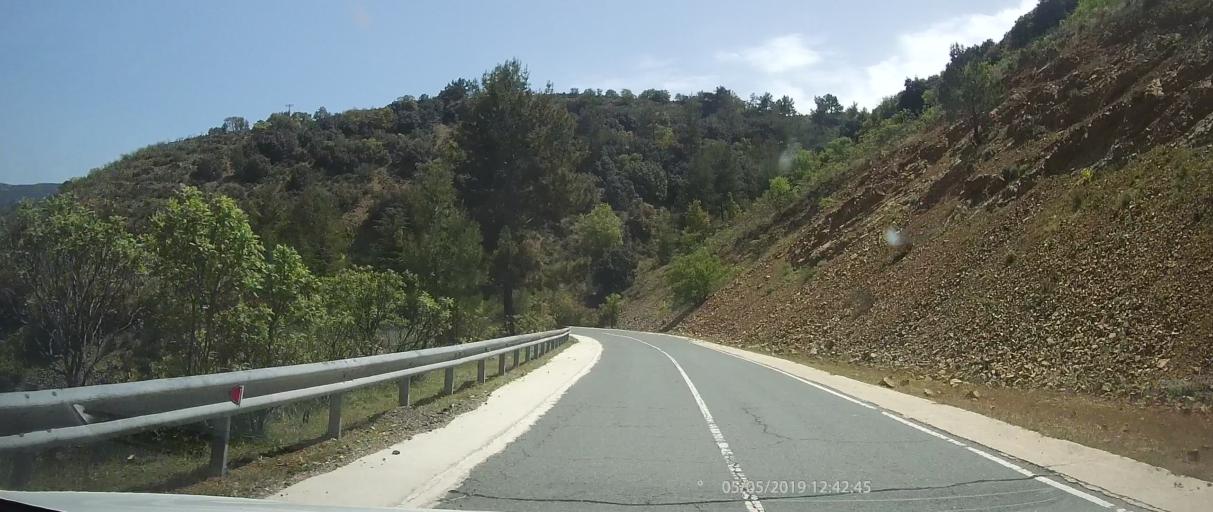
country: CY
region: Lefkosia
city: Kakopetria
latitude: 34.9713
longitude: 32.8120
